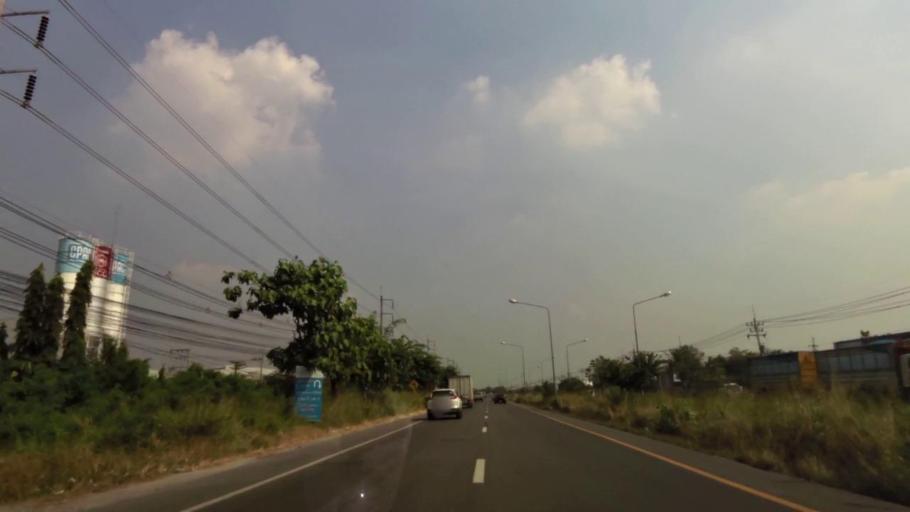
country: TH
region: Chon Buri
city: Ban Bueng
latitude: 13.3011
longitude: 101.1459
